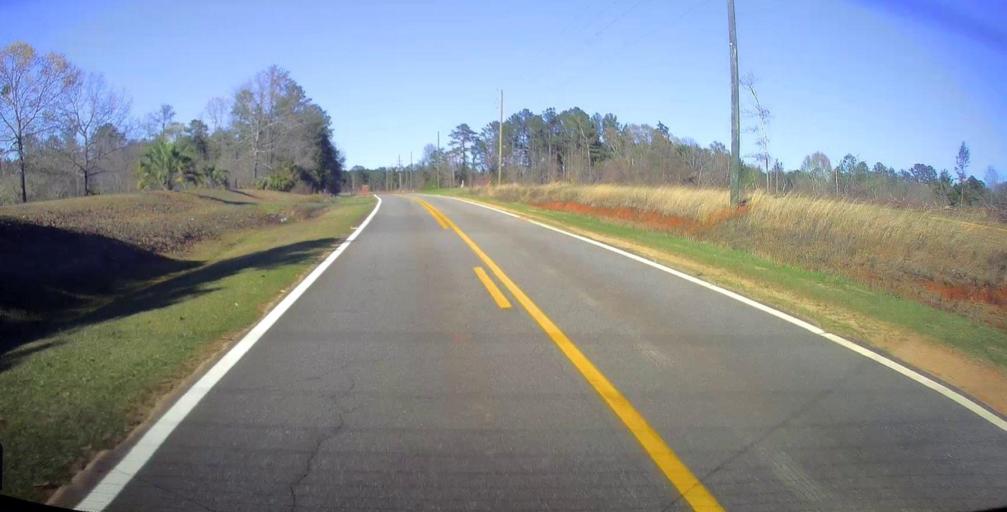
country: US
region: Georgia
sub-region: Peach County
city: Fort Valley
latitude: 32.5833
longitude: -83.9907
